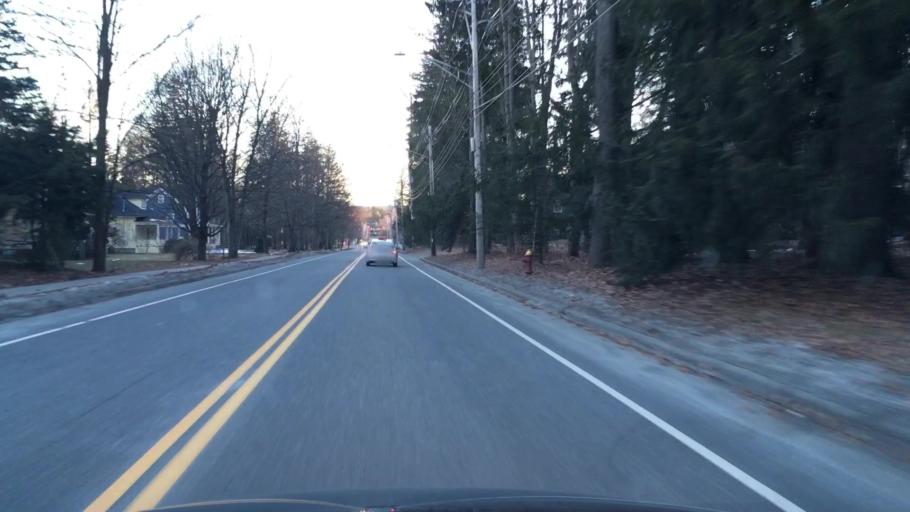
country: US
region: New Hampshire
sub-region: Grafton County
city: Hanover
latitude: 43.7069
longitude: -72.2830
